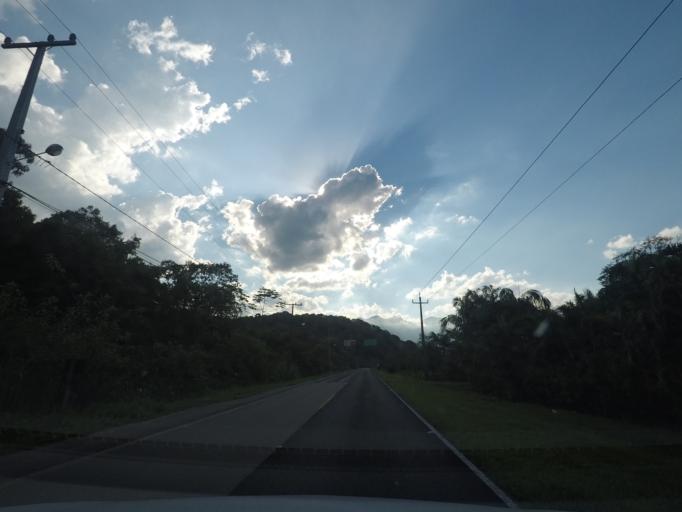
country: BR
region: Parana
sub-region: Antonina
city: Antonina
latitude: -25.4459
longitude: -48.8727
